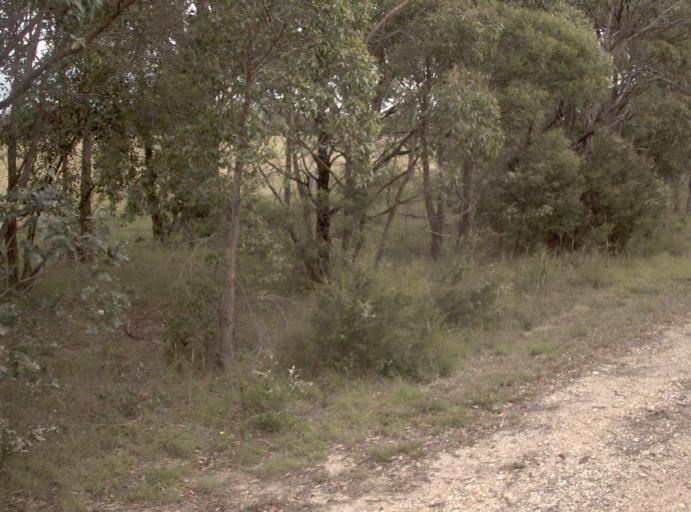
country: AU
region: Victoria
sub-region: East Gippsland
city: Bairnsdale
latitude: -37.7961
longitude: 147.3648
